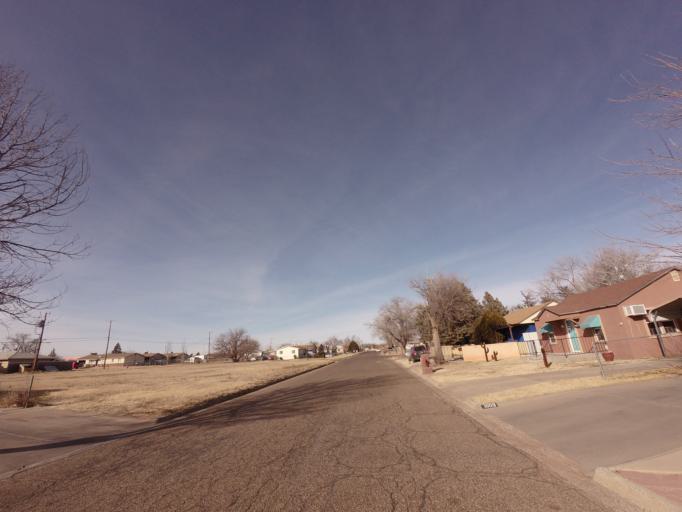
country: US
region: New Mexico
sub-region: Curry County
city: Clovis
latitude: 34.4083
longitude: -103.2217
